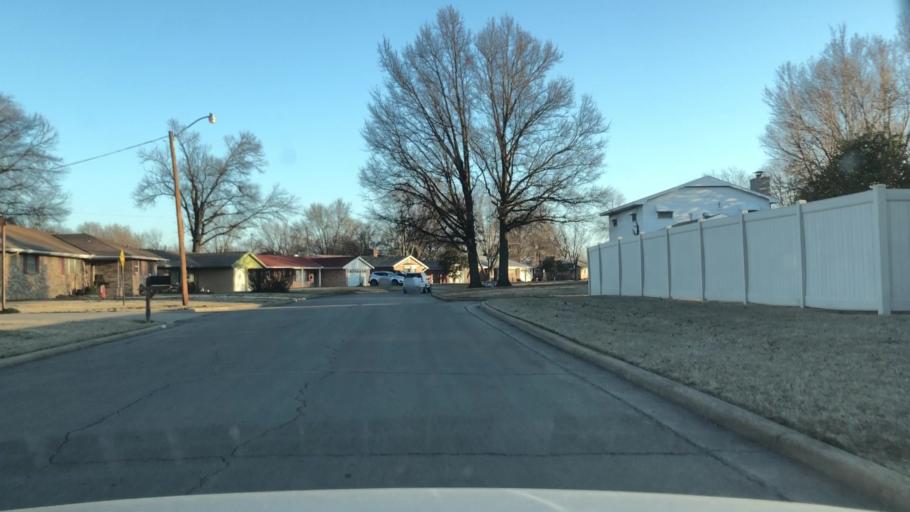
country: US
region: Oklahoma
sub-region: Washington County
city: Dewey
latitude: 36.7821
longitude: -95.9407
